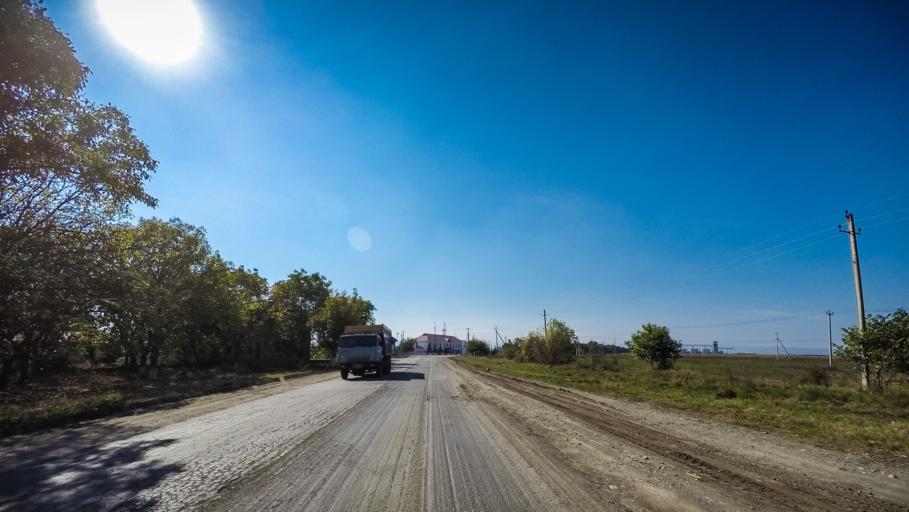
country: RU
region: Kabardino-Balkariya
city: Chegem Vtoroy
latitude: 43.5799
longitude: 43.5794
